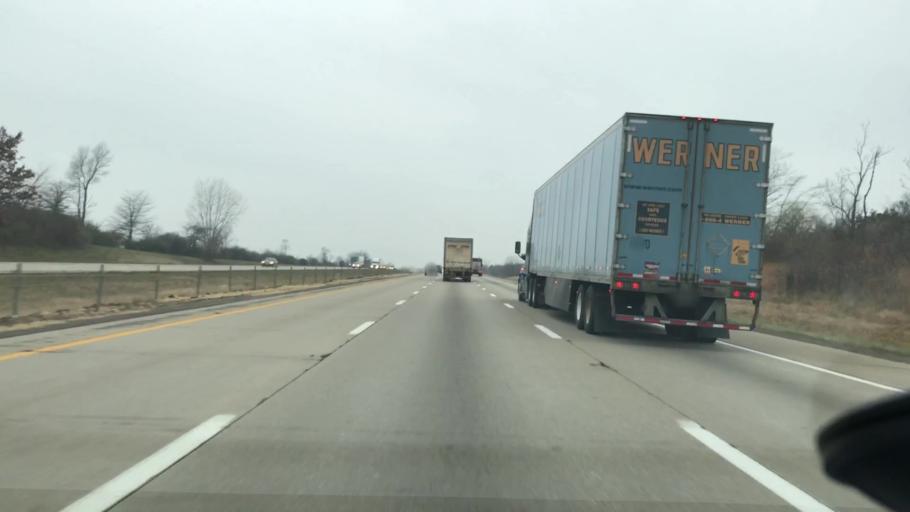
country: US
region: Ohio
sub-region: Madison County
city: West Jefferson
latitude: 39.9627
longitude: -83.3144
